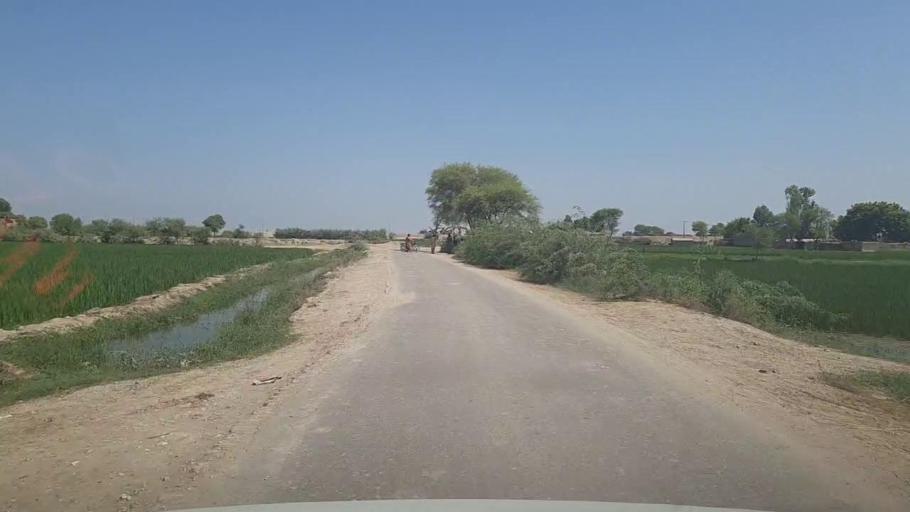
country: PK
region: Sindh
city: Kashmor
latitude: 28.2815
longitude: 69.4413
